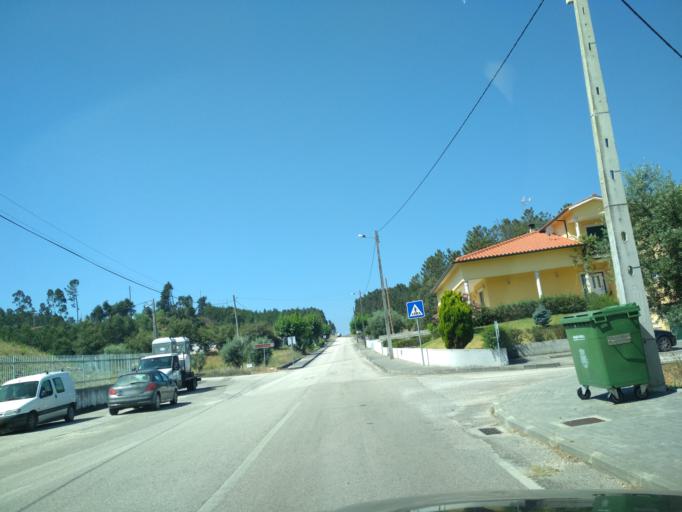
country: PT
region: Coimbra
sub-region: Soure
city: Soure
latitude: 40.0034
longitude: -8.5903
